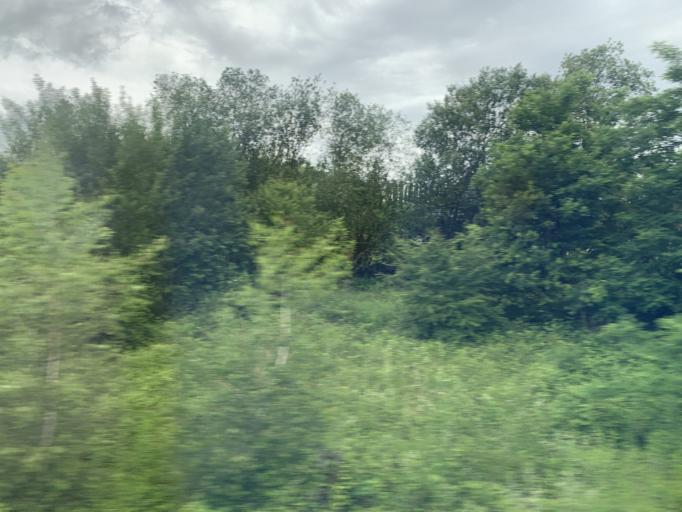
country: FR
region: Alsace
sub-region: Departement du Haut-Rhin
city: Dannemarie
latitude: 47.6283
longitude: 7.1297
